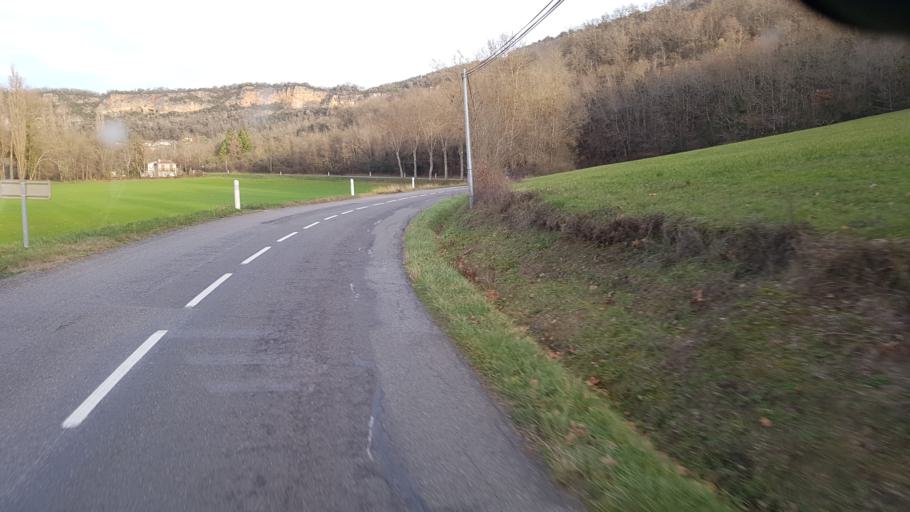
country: FR
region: Midi-Pyrenees
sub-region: Departement du Tarn-et-Garonne
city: Montricoux
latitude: 43.9971
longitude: 1.6969
